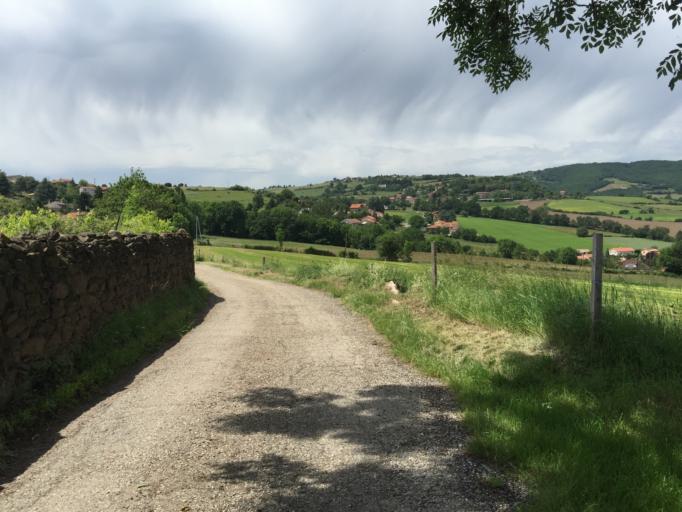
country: FR
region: Rhone-Alpes
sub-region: Departement de la Loire
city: Saint-Chamond
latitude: 45.4851
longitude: 4.4963
